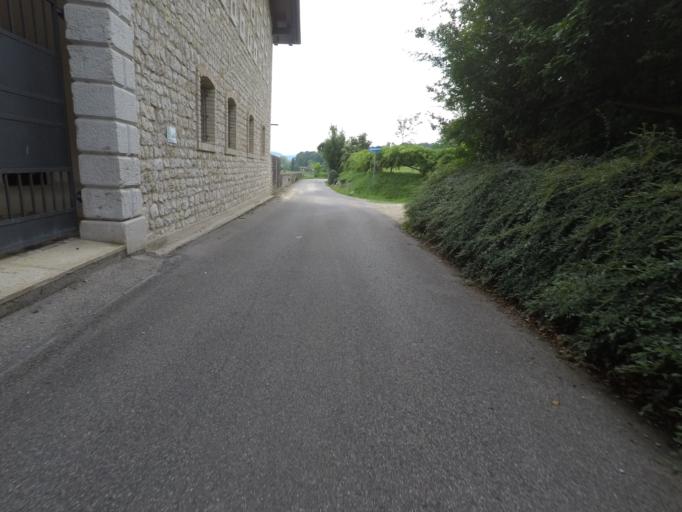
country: IT
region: Friuli Venezia Giulia
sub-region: Provincia di Pordenone
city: San Giovanni
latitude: 46.0220
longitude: 12.5034
